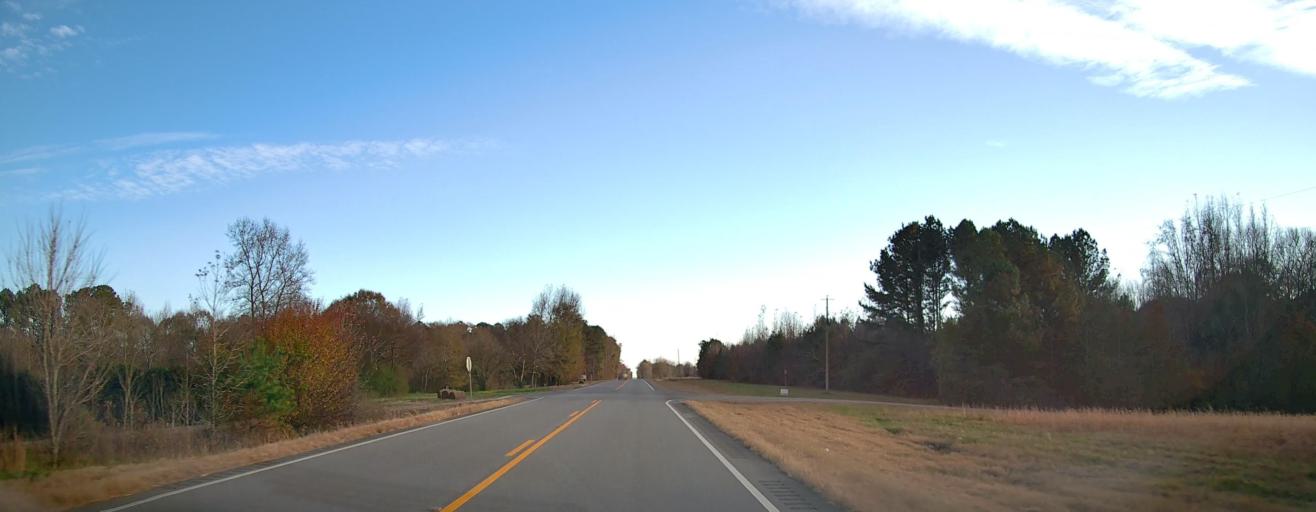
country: US
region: Alabama
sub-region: Marshall County
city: Arab
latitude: 34.2769
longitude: -86.5819
